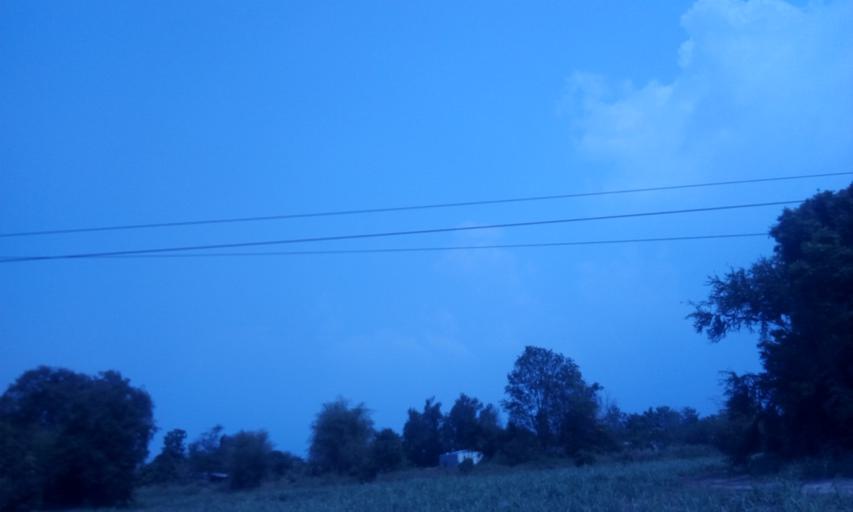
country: TH
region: Chon Buri
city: Phanat Nikhom
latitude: 13.3677
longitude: 101.1958
